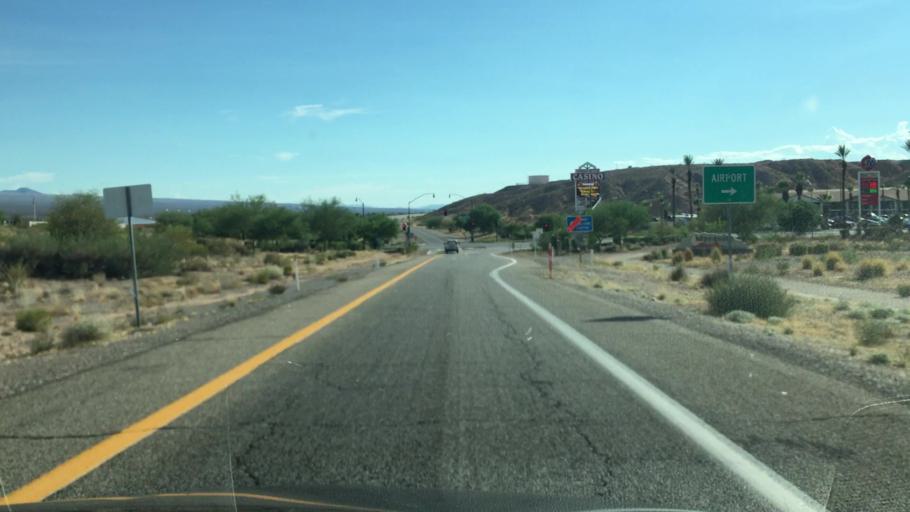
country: US
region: Nevada
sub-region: Clark County
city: Mesquite
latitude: 36.8146
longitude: -114.0631
